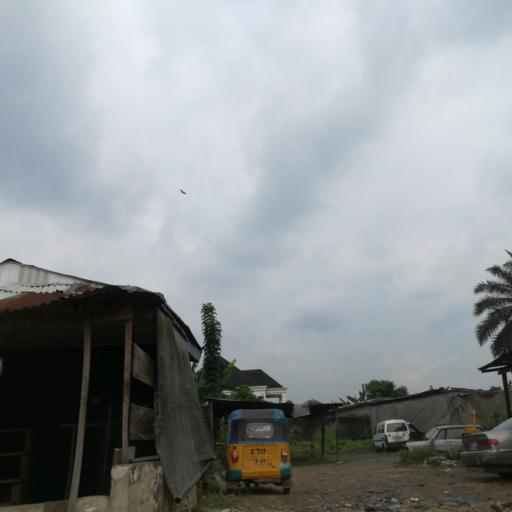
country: NG
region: Rivers
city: Port Harcourt
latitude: 4.8411
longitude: 7.0753
